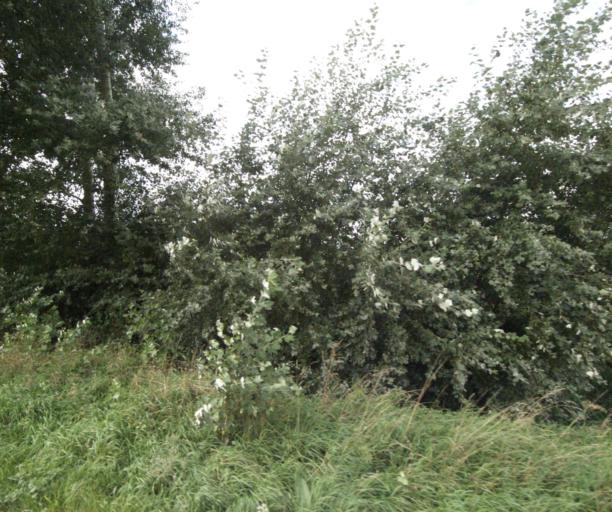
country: FR
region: Nord-Pas-de-Calais
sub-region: Departement du Nord
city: Premesques
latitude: 50.6664
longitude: 2.9406
